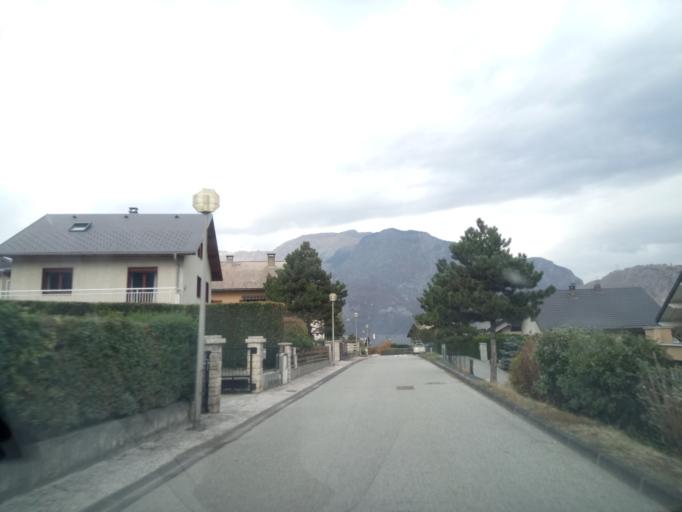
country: FR
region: Rhone-Alpes
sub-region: Departement de la Savoie
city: Villargondran
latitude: 45.2628
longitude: 6.3801
